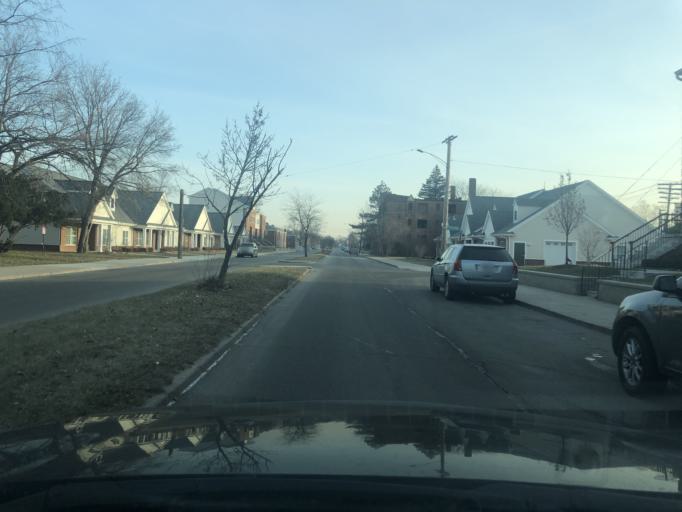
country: US
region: Michigan
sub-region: Wayne County
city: Highland Park
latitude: 42.3919
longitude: -83.1384
